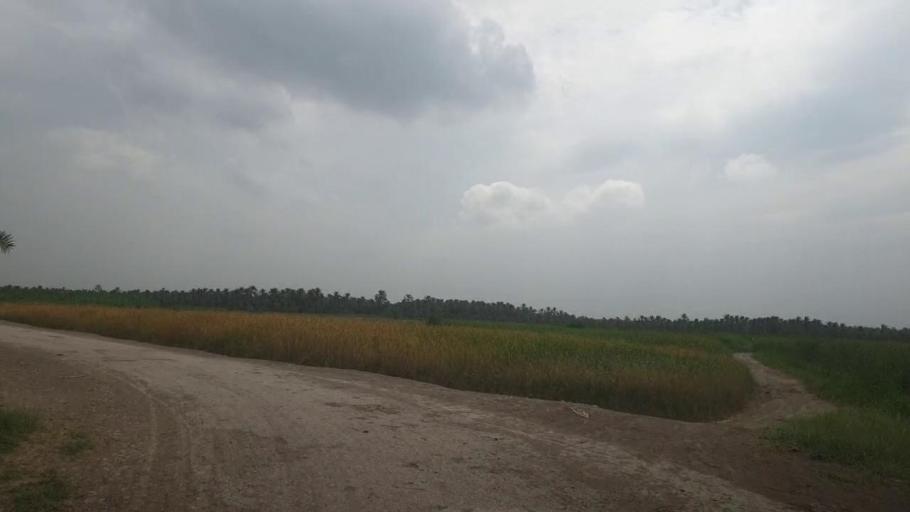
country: PK
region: Sindh
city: Khairpur
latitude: 27.5872
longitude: 68.7394
